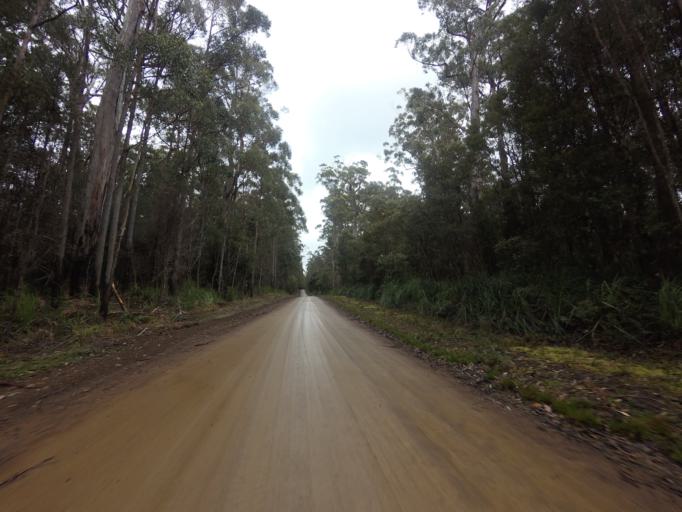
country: AU
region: Tasmania
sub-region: Huon Valley
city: Geeveston
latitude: -43.5279
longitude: 146.8895
